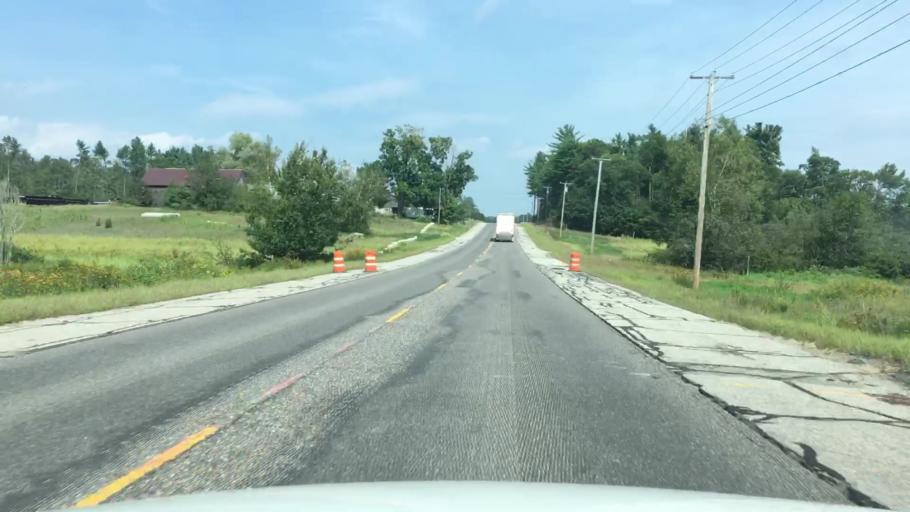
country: US
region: Maine
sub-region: Androscoggin County
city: Livermore
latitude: 44.3215
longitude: -70.2605
